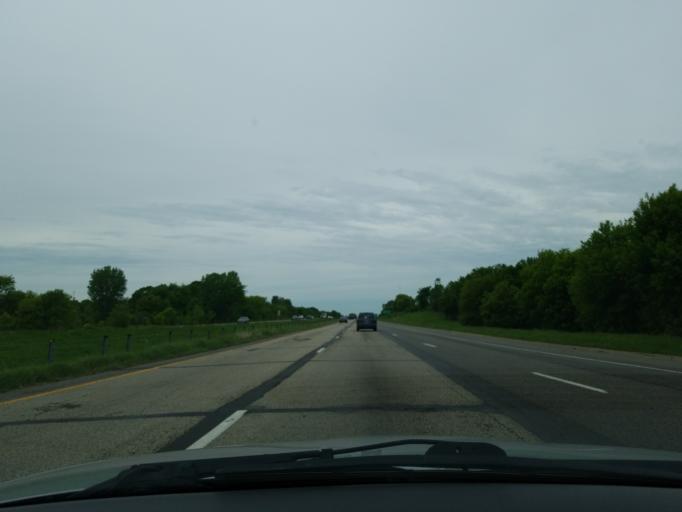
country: US
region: Minnesota
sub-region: Sherburne County
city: Big Lake
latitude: 45.2765
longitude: -93.7379
